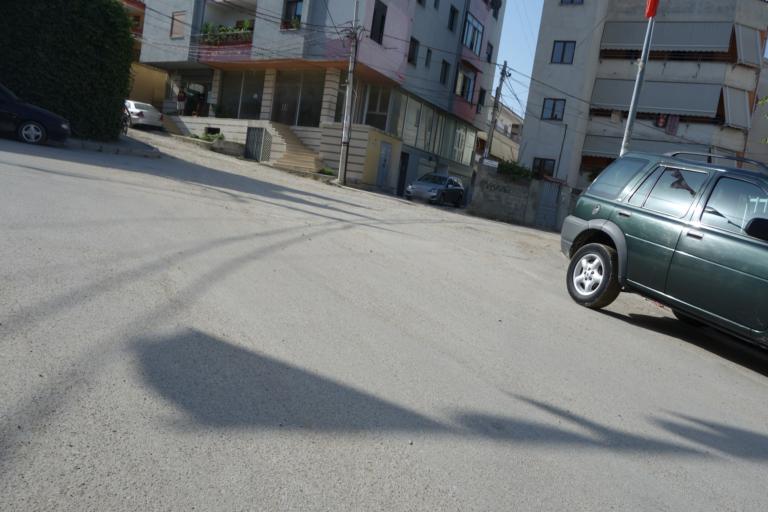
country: AL
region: Tirane
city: Tirana
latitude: 41.3393
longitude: 19.8497
